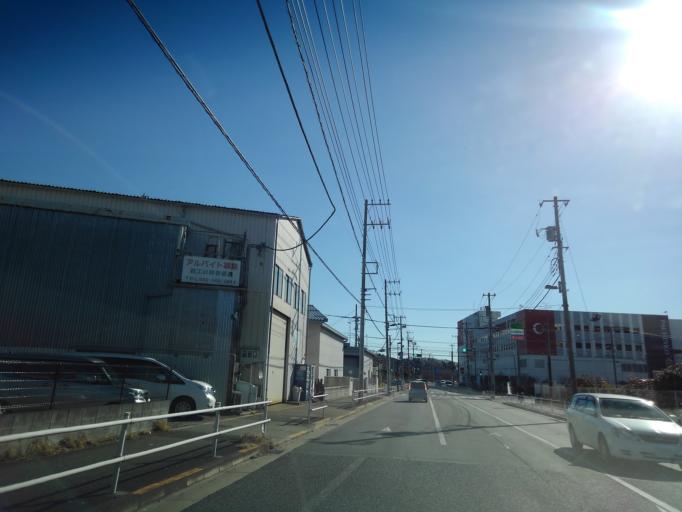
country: JP
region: Tokyo
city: Fussa
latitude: 35.7865
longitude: 139.3471
